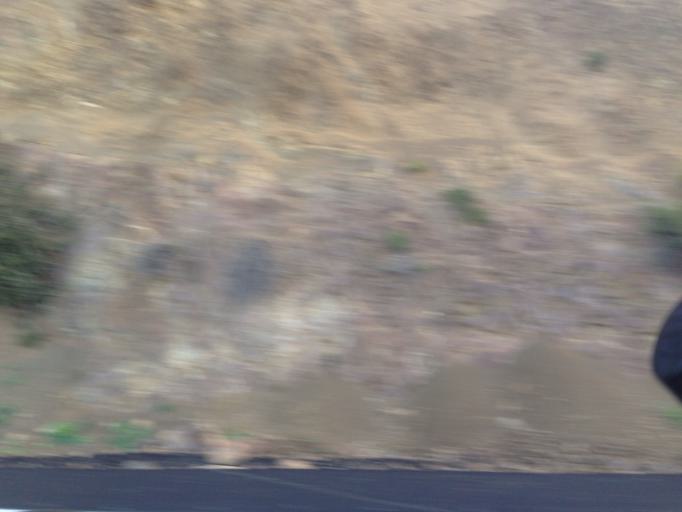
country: MX
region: Baja California
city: Primo Tapia
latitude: 32.1617
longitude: -116.8971
